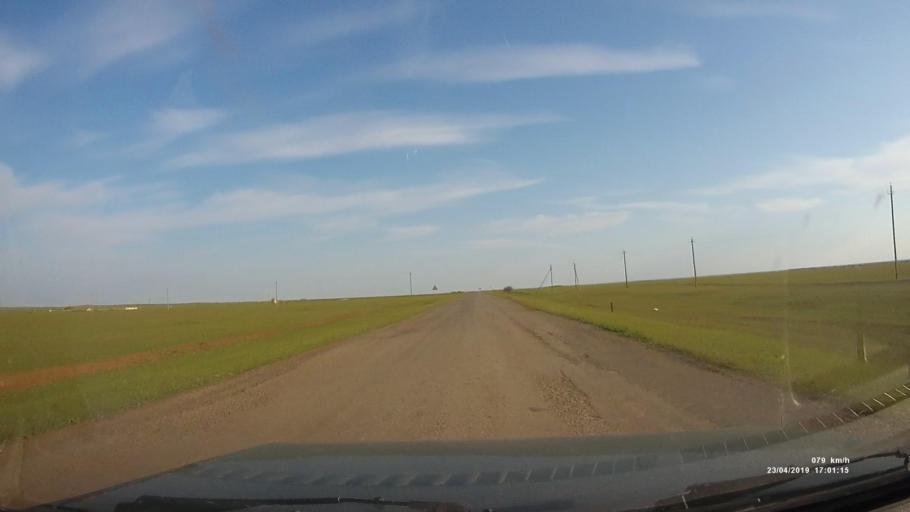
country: RU
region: Kalmykiya
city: Priyutnoye
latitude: 46.2982
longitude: 43.4074
